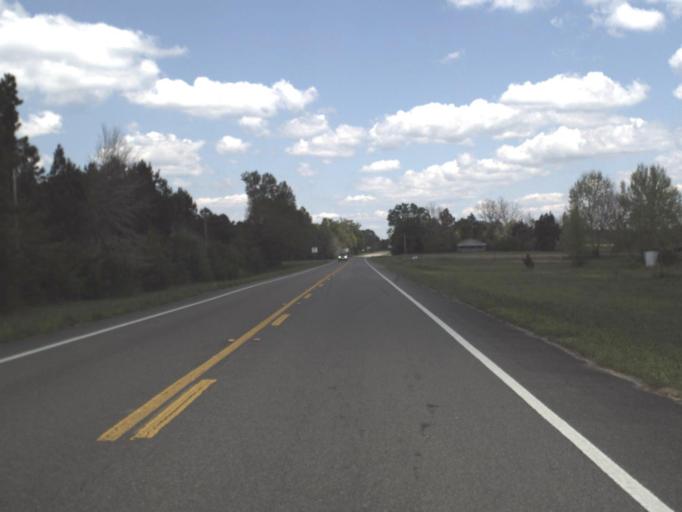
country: US
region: Florida
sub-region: Okaloosa County
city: Crestview
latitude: 30.9856
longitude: -86.6297
